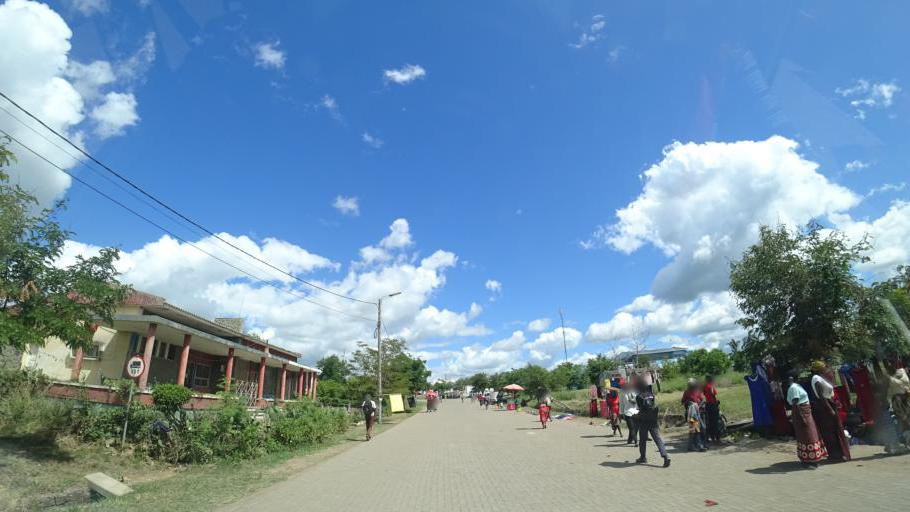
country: MZ
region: Sofala
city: Dondo
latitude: -19.2717
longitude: 34.2067
